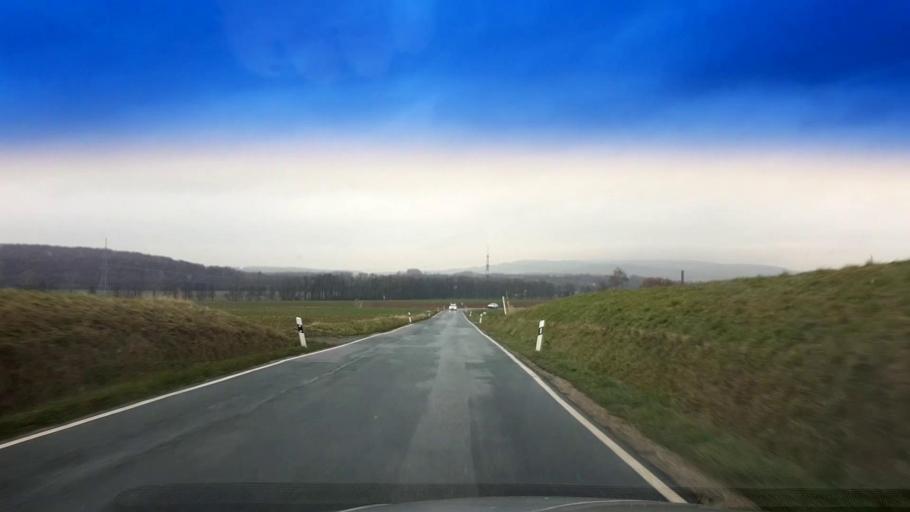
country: DE
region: Bavaria
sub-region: Upper Franconia
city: Schesslitz
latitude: 49.9599
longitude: 11.0188
